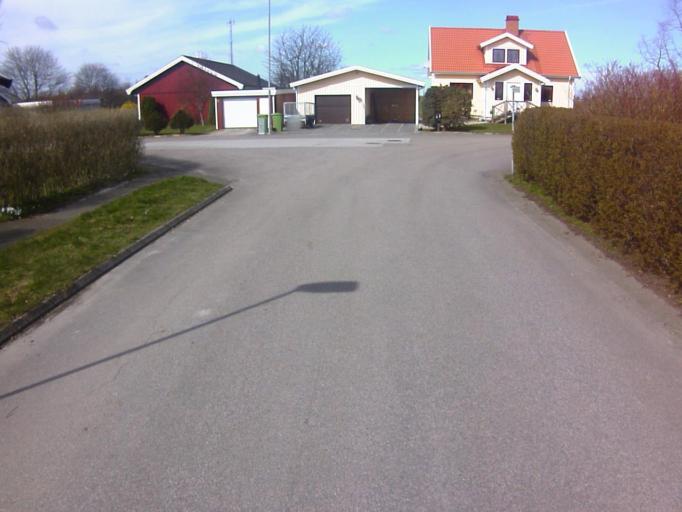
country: SE
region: Skane
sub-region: Kavlinge Kommun
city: Kaevlinge
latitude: 55.8068
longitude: 13.1126
